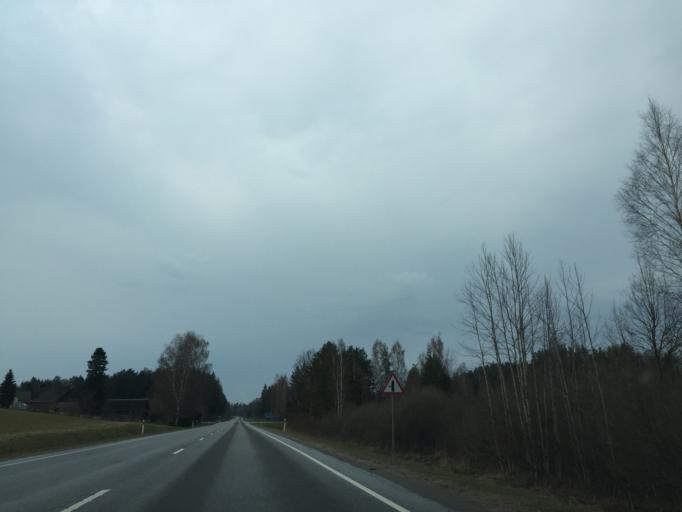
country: EE
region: Tartu
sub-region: UElenurme vald
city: Ulenurme
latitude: 58.1128
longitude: 26.7361
